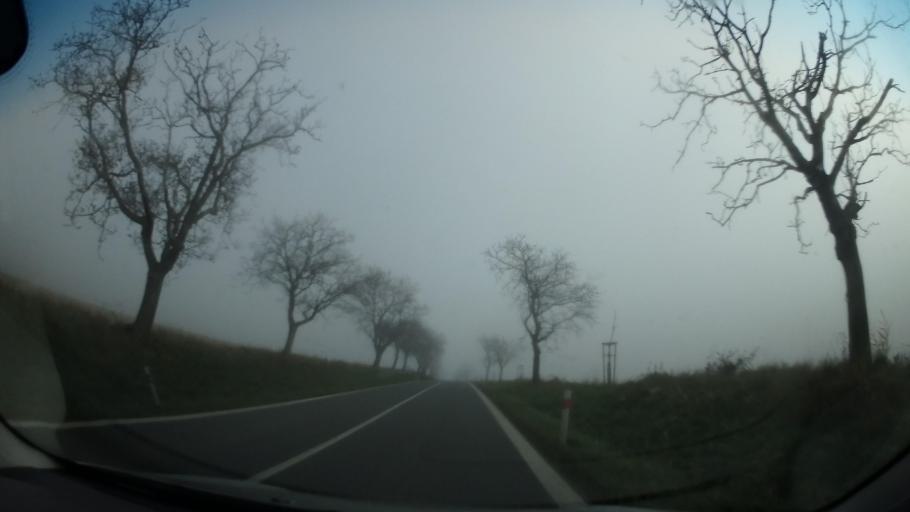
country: CZ
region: South Moravian
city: Zdanice
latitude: 49.0447
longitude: 16.9896
